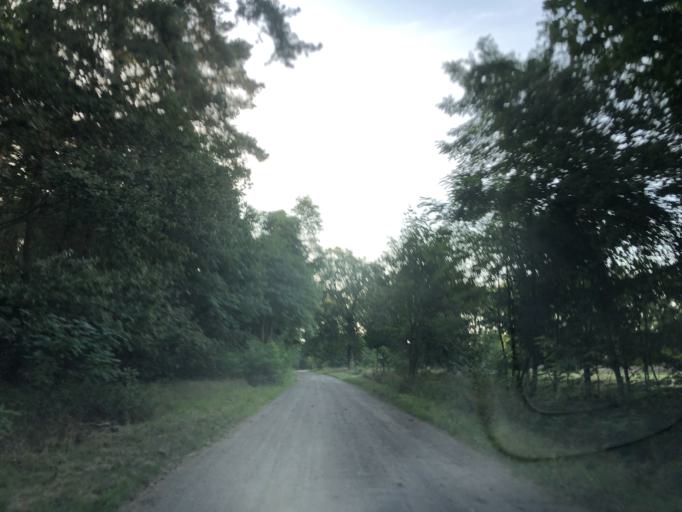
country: PL
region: Lubusz
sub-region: Powiat swiebodzinski
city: Zbaszynek
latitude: 52.2380
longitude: 15.7825
